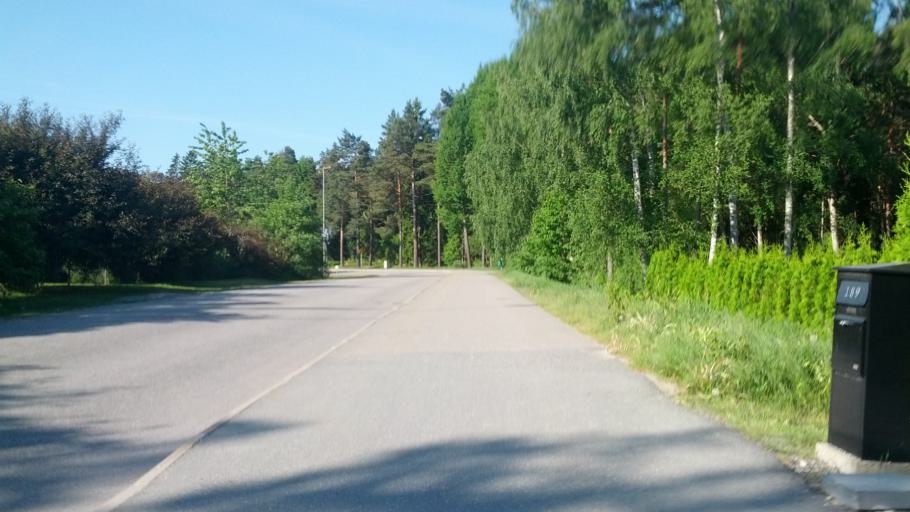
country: SE
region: Stockholm
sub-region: Taby Kommun
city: Taby
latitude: 59.4684
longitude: 18.0478
